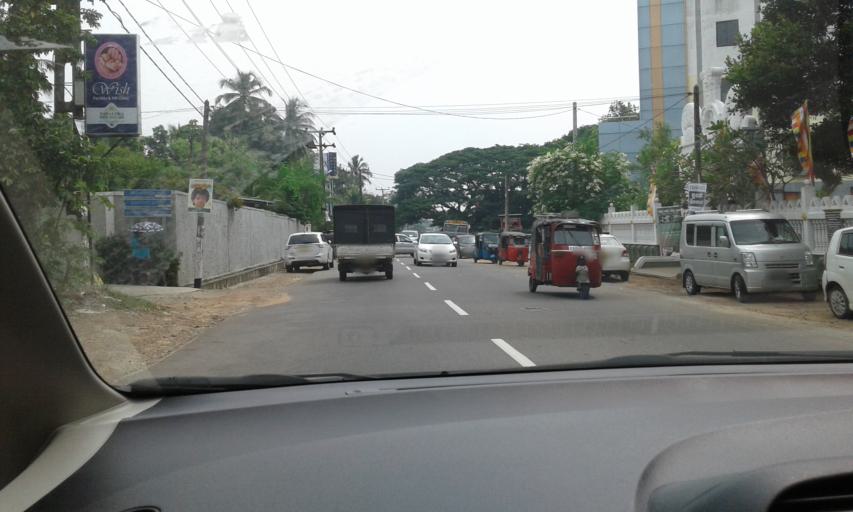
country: LK
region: Western
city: Sri Jayewardenepura Kotte
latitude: 6.8659
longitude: 79.9116
